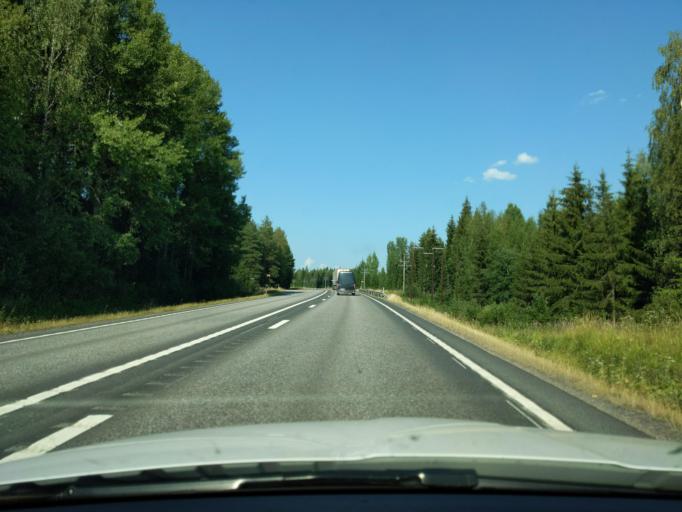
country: FI
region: Paijanne Tavastia
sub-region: Lahti
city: Jaervelae
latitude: 60.9139
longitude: 25.3504
